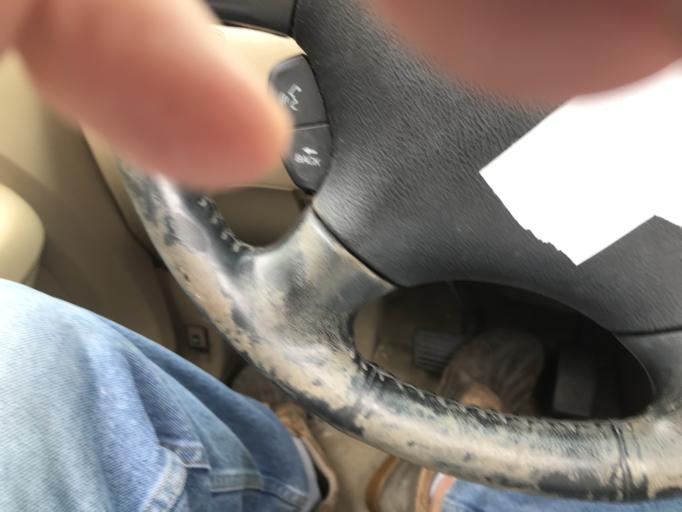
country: US
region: Louisiana
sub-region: Orleans Parish
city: New Orleans
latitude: 29.9416
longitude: -90.0657
